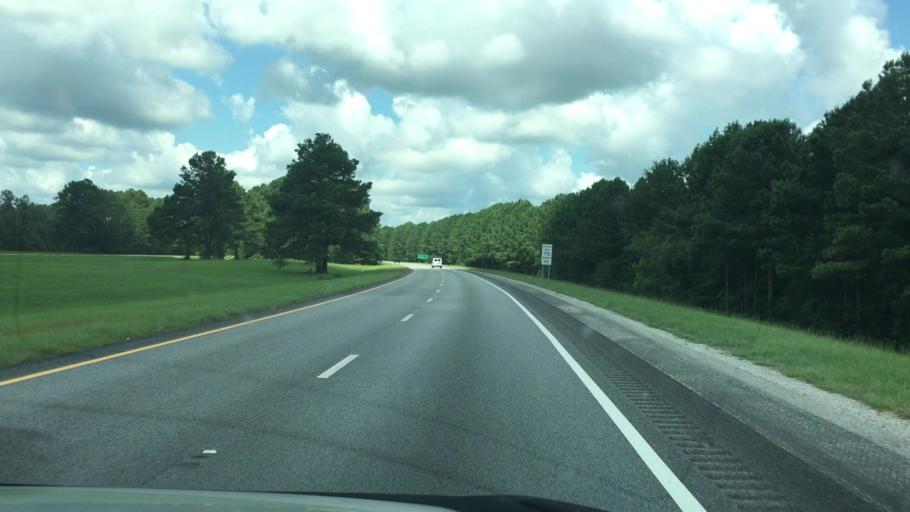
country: US
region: South Carolina
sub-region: Florence County
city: Timmonsville
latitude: 34.2072
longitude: -79.9254
